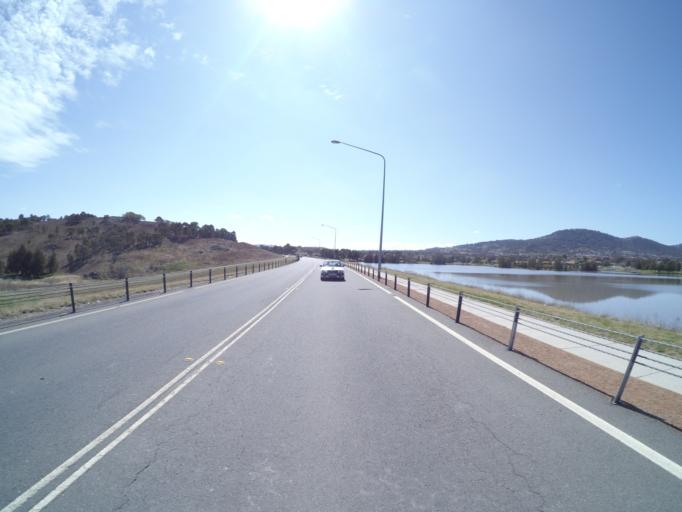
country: AU
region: Australian Capital Territory
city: Macarthur
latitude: -35.4551
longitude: 149.0789
